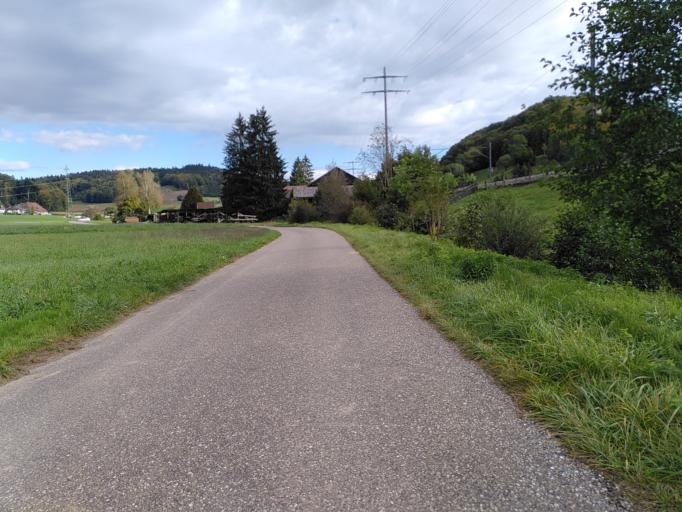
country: CH
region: Bern
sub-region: Emmental District
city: Wynigen
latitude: 47.1232
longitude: 7.6735
